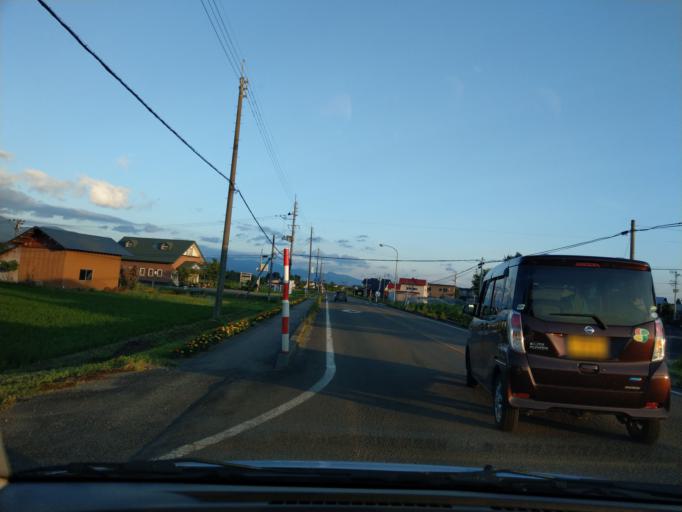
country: JP
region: Akita
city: Kakunodatemachi
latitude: 39.6417
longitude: 140.5715
